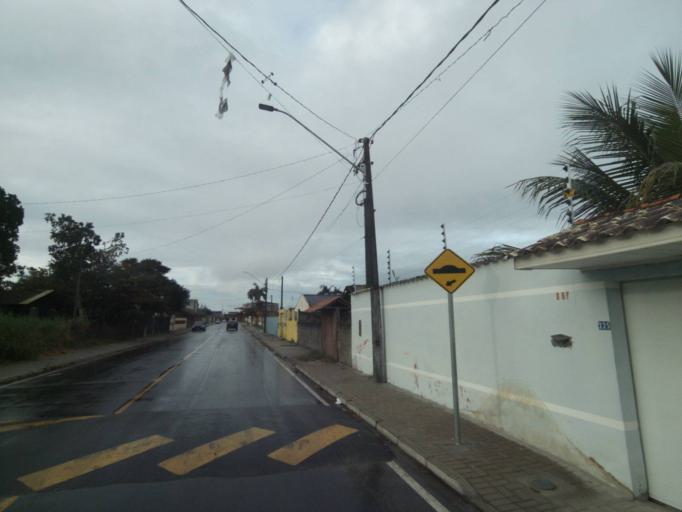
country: BR
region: Parana
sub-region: Paranagua
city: Paranagua
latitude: -25.5717
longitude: -48.5731
